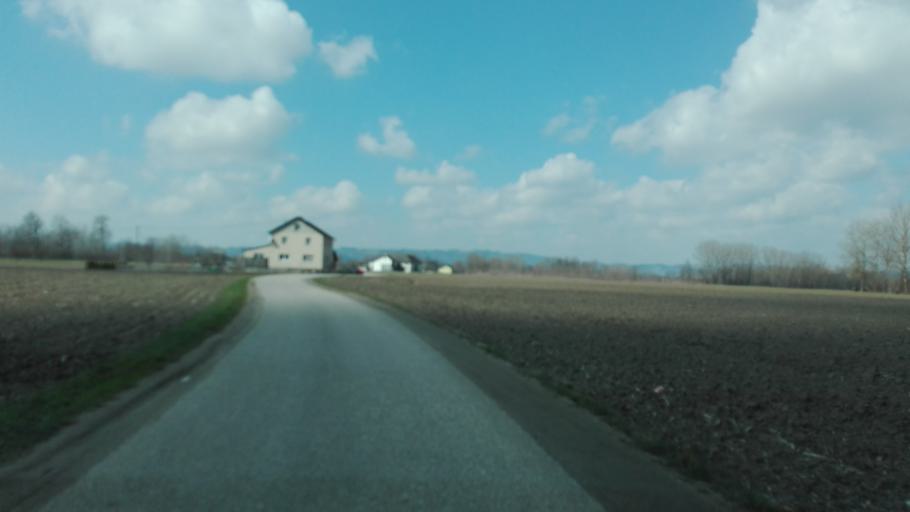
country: AT
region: Upper Austria
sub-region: Politischer Bezirk Urfahr-Umgebung
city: Goldworth
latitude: 48.3290
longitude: 14.0868
